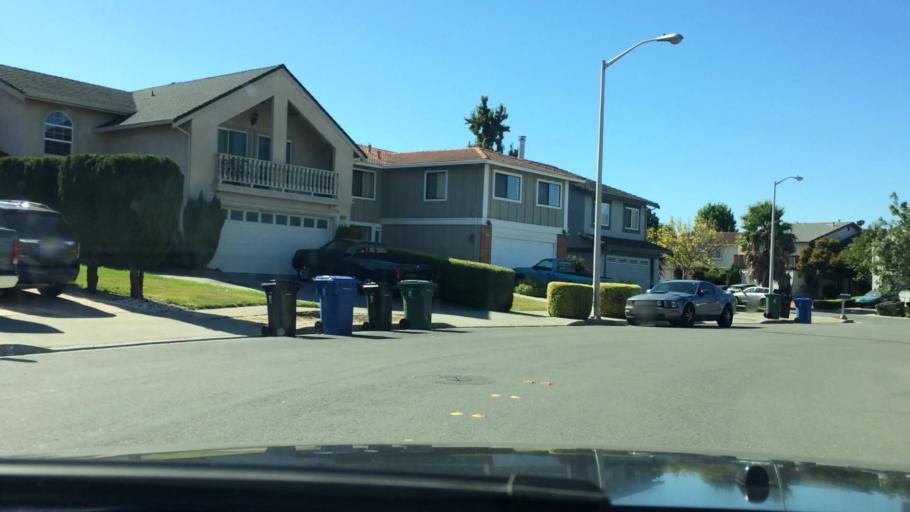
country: US
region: California
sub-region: Alameda County
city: Newark
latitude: 37.5413
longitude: -122.0521
